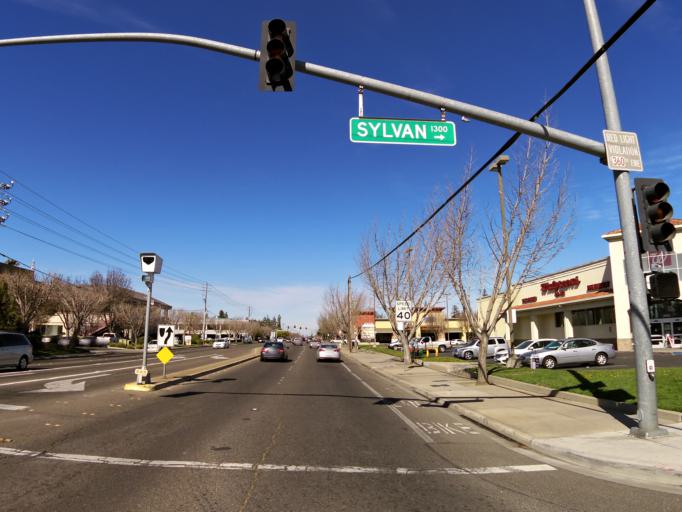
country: US
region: California
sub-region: Stanislaus County
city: Modesto
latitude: 37.6890
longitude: -120.9760
